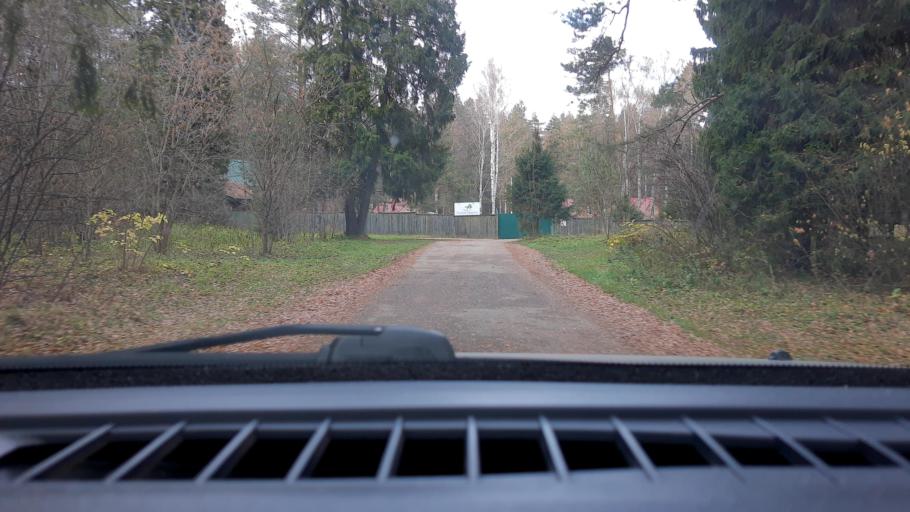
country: RU
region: Nizjnij Novgorod
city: Kstovo
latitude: 56.1704
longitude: 44.1327
